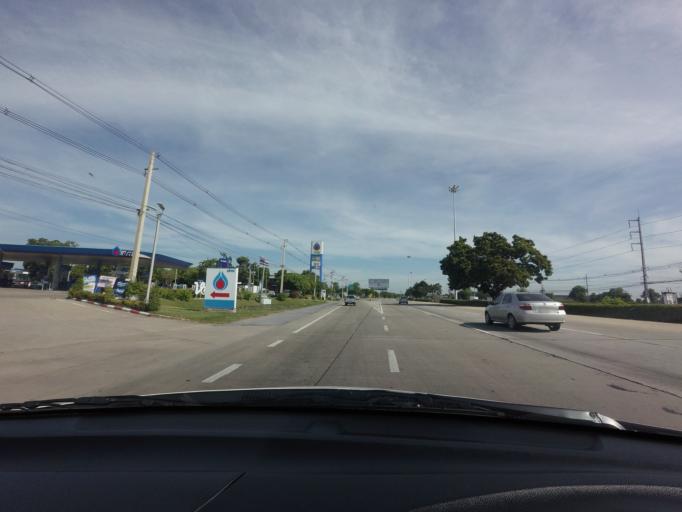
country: TH
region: Suphan Buri
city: Suphan Buri
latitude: 14.4424
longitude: 100.1335
